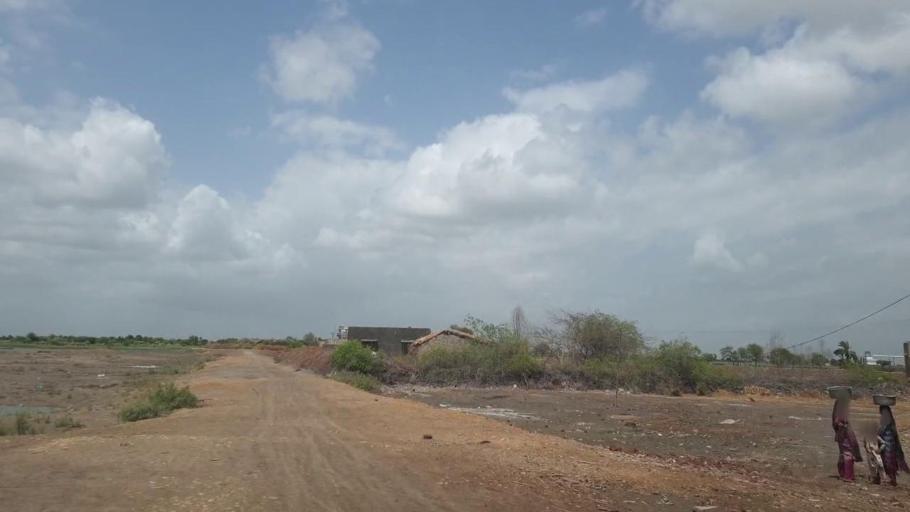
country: PK
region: Sindh
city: Badin
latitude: 24.6591
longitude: 68.9555
